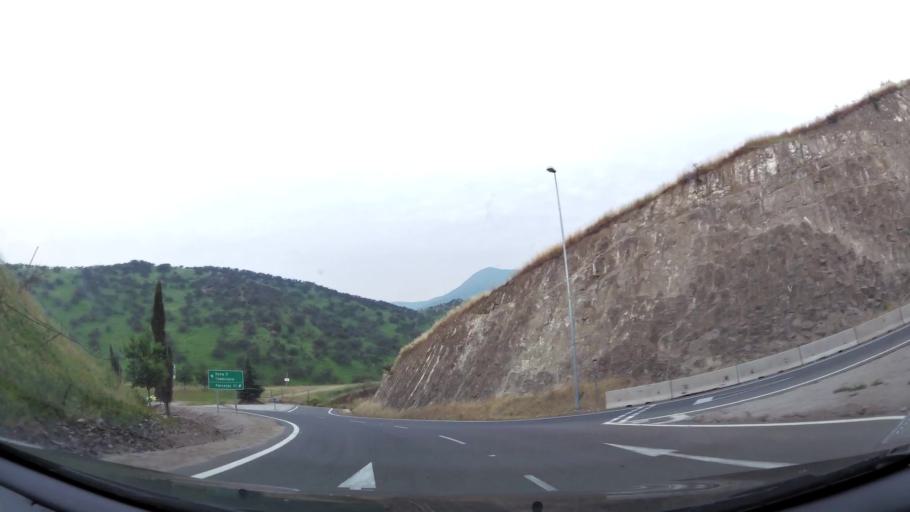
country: CL
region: Santiago Metropolitan
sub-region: Provincia de Chacabuco
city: Chicureo Abajo
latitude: -33.3220
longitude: -70.6251
